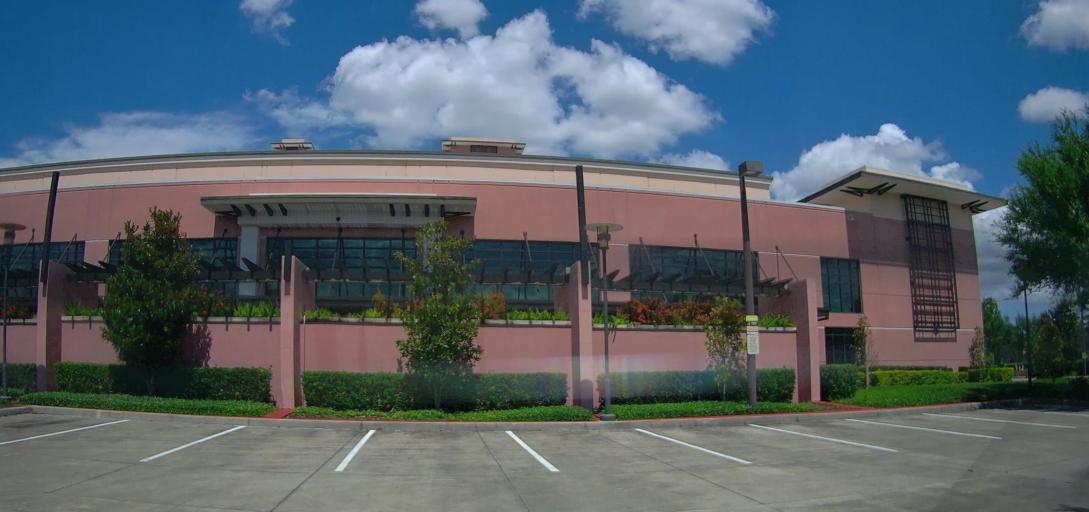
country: US
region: Florida
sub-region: Osceola County
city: Celebration
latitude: 28.3360
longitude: -81.4820
